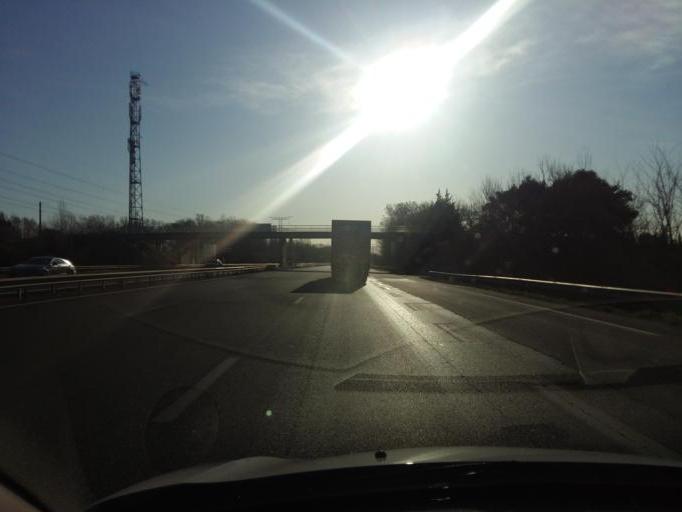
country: FR
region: Provence-Alpes-Cote d'Azur
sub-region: Departement des Bouches-du-Rhone
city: Cabannes
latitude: 43.8743
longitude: 4.9515
